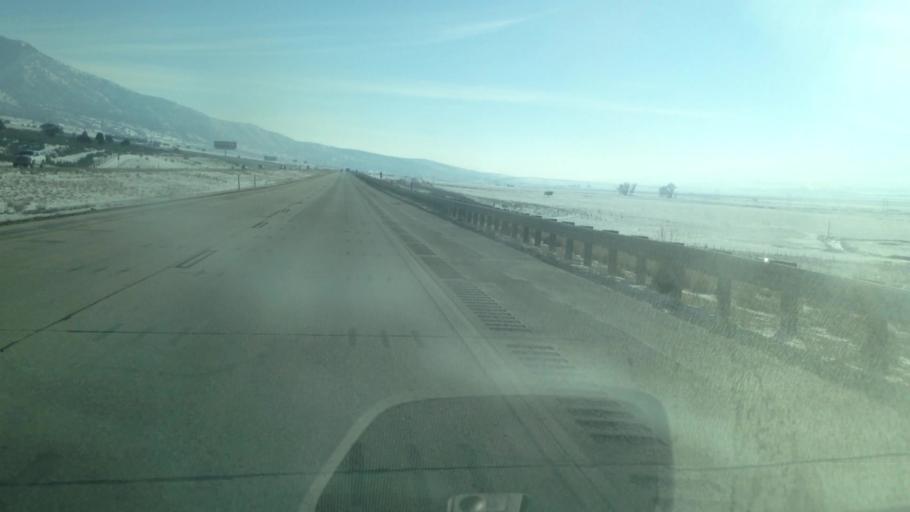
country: US
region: Utah
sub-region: Box Elder County
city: Garland
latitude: 41.9542
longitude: -112.1783
